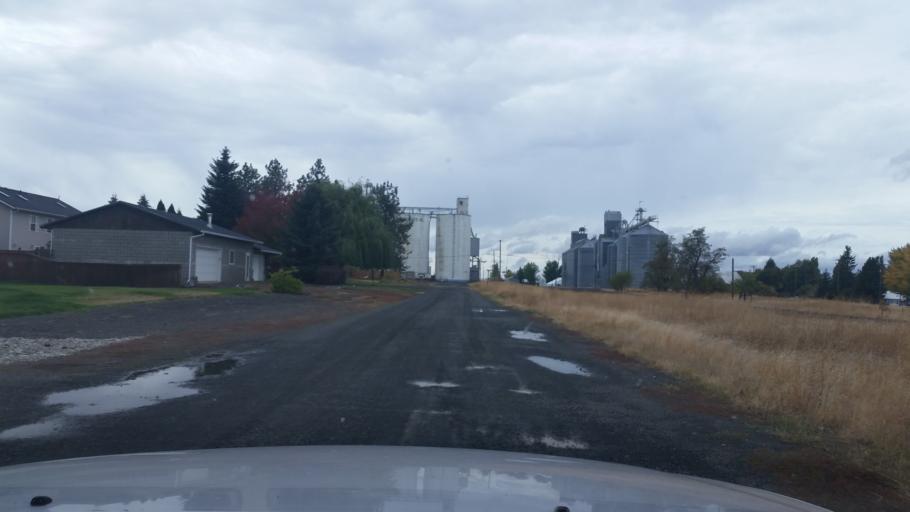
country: US
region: Washington
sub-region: Spokane County
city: Medical Lake
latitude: 47.6706
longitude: -117.8751
